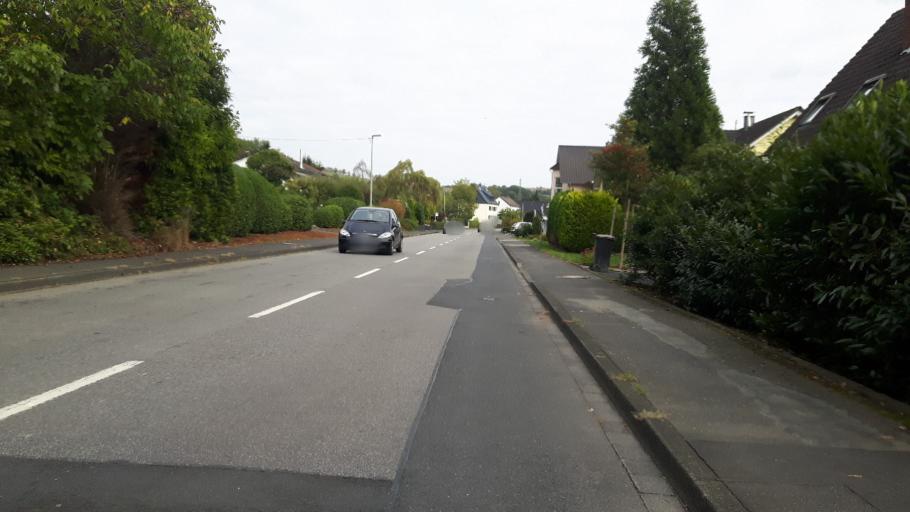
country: DE
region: North Rhine-Westphalia
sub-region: Regierungsbezirk Koln
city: Eitorf
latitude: 50.7777
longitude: 7.4608
